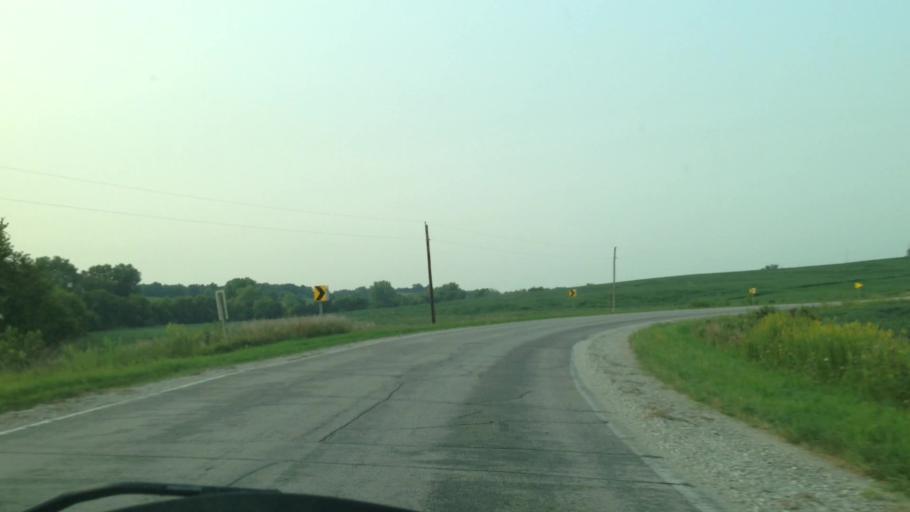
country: US
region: Iowa
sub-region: Iowa County
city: Marengo
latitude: 41.8612
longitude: -92.0915
